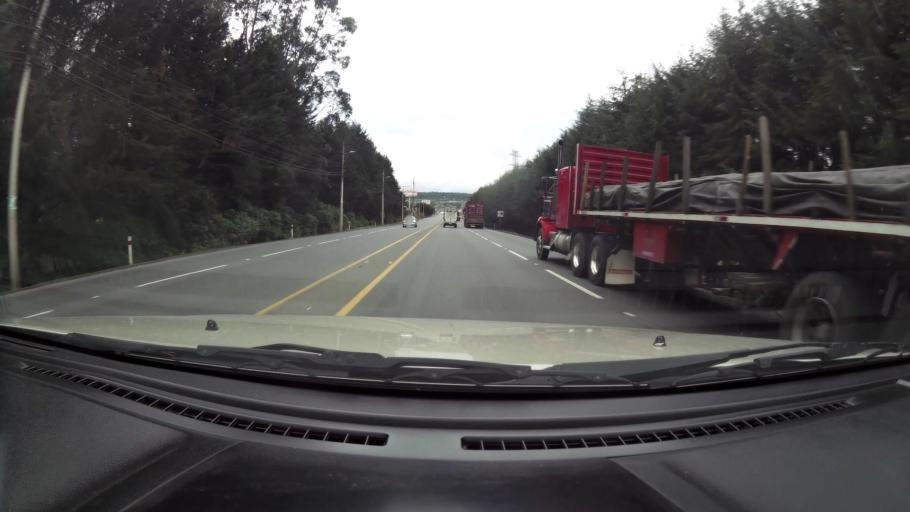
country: EC
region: Pichincha
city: Machachi
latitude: -0.4447
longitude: -78.6034
